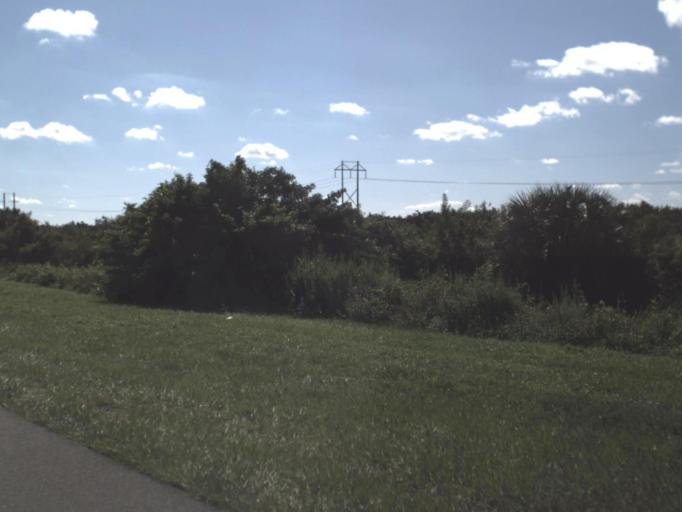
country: US
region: Florida
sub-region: Lee County
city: Lehigh Acres
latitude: 26.5243
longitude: -81.5868
